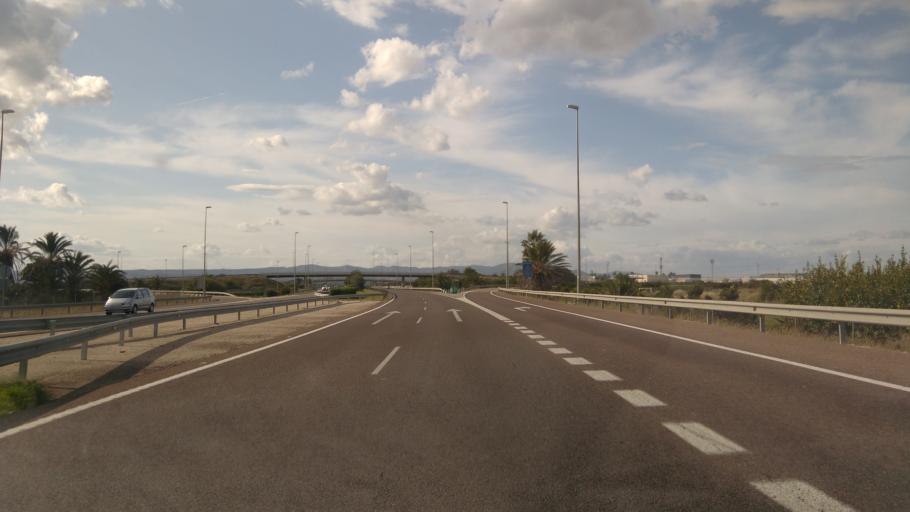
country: ES
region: Valencia
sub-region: Provincia de Valencia
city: Guadassuar
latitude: 39.1765
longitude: -0.4722
